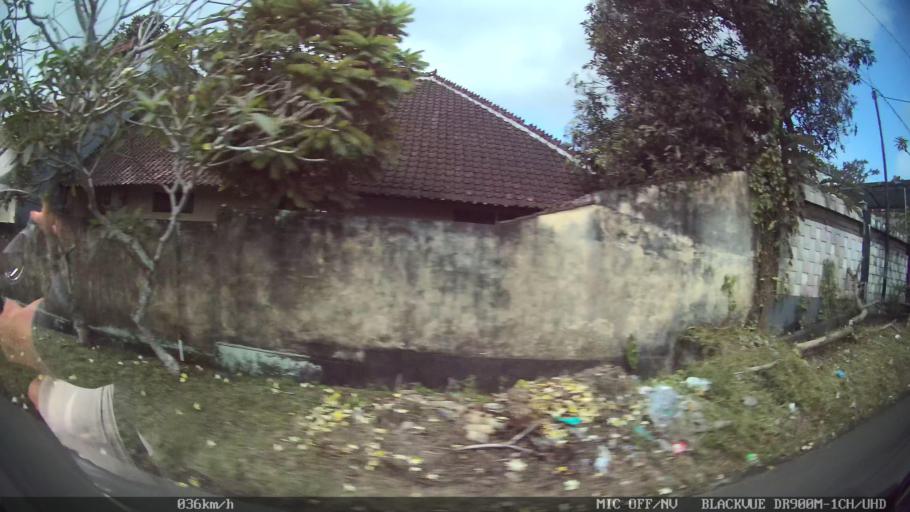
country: ID
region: Bali
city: Banjar Pesalakan
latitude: -8.5148
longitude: 115.3021
